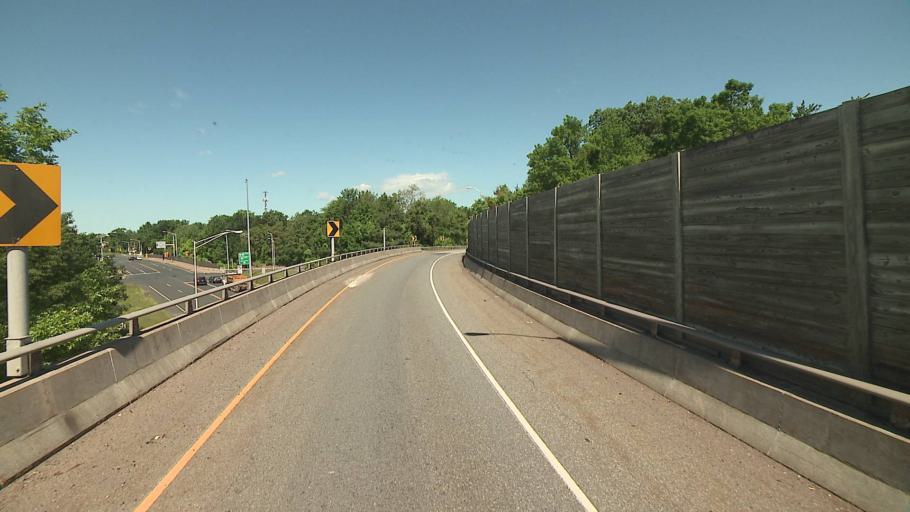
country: US
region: Connecticut
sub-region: Hartford County
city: Blue Hills
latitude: 41.8194
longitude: -72.6630
